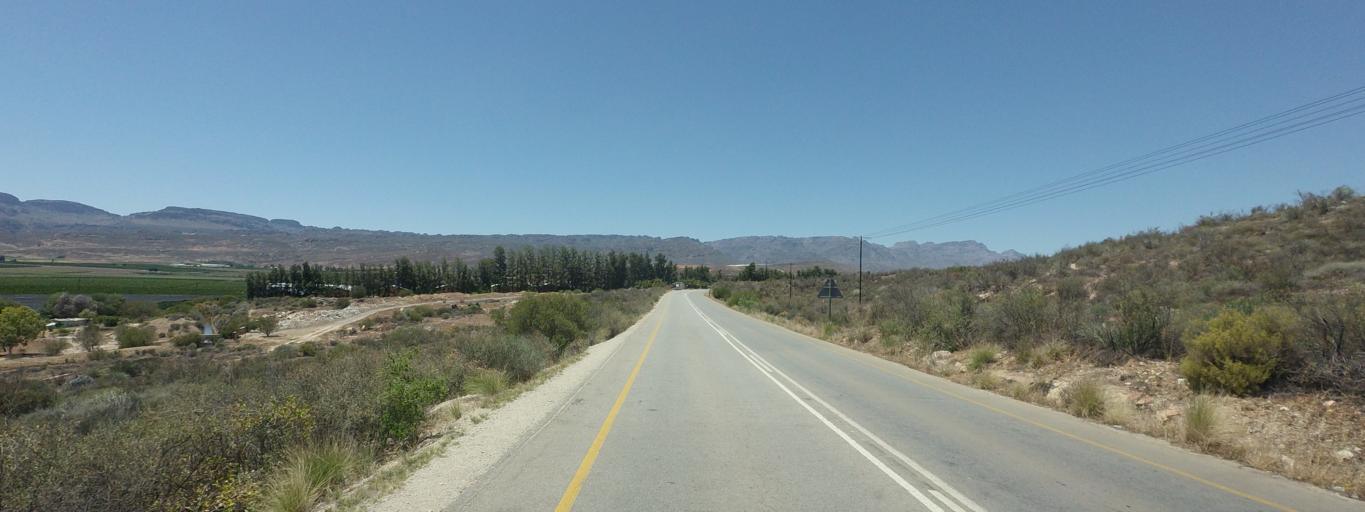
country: ZA
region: Western Cape
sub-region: West Coast District Municipality
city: Clanwilliam
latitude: -32.1701
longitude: 18.8766
